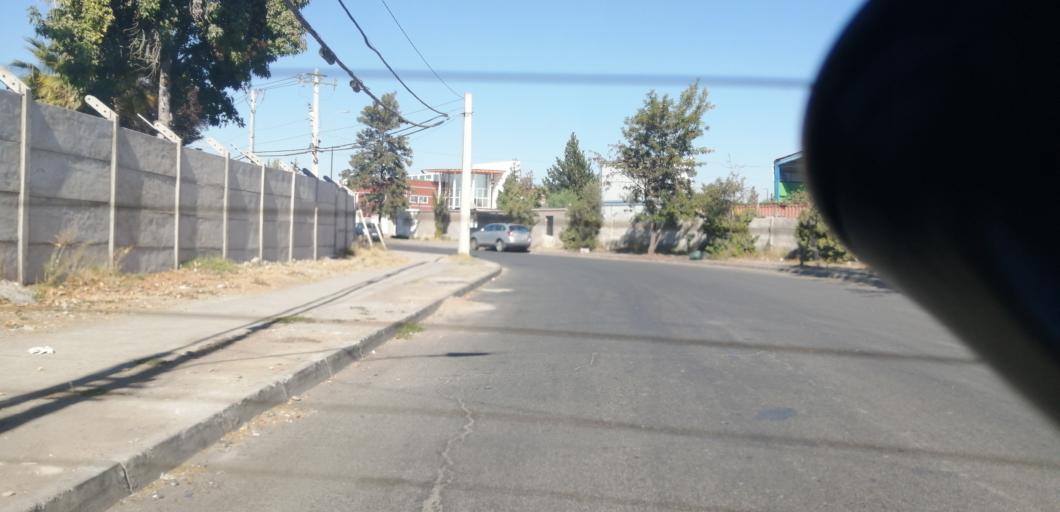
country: CL
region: Santiago Metropolitan
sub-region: Provincia de Santiago
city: Lo Prado
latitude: -33.4481
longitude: -70.7774
